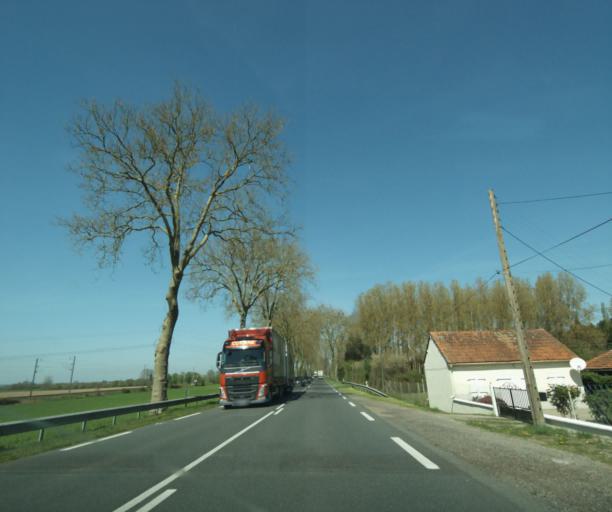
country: FR
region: Bourgogne
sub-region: Departement de la Nievre
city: Chantenay-Saint-Imbert
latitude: 46.6892
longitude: 3.2176
